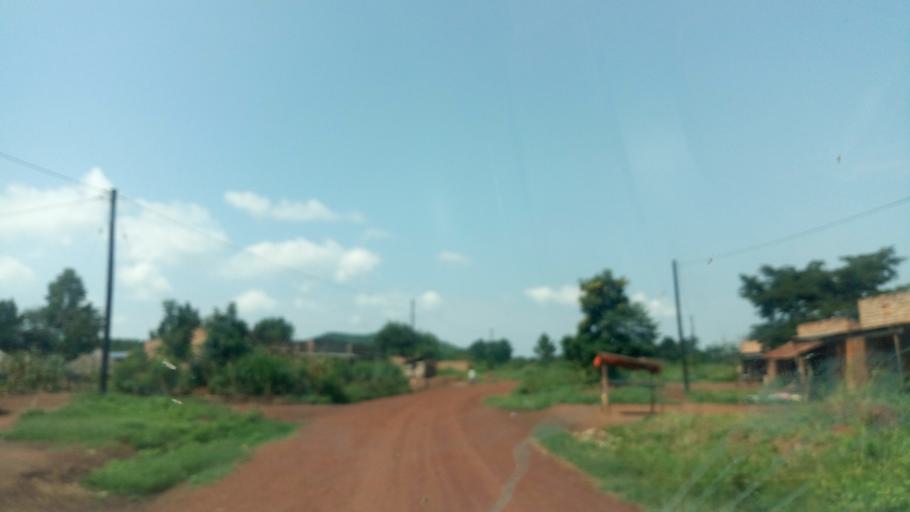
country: UG
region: Western Region
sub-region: Masindi District
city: Masindi
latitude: 1.6860
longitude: 31.8354
